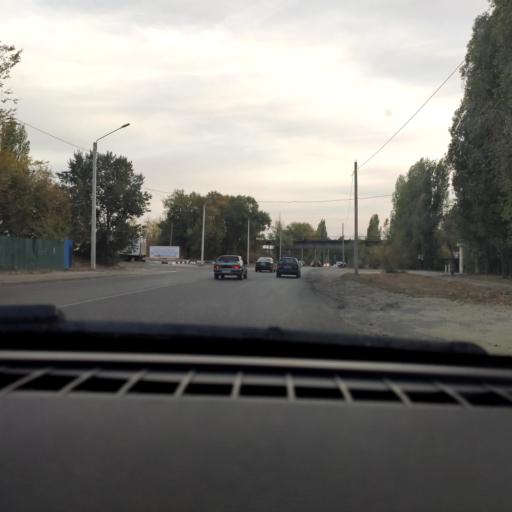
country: RU
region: Voronezj
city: Maslovka
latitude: 51.6269
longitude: 39.2617
